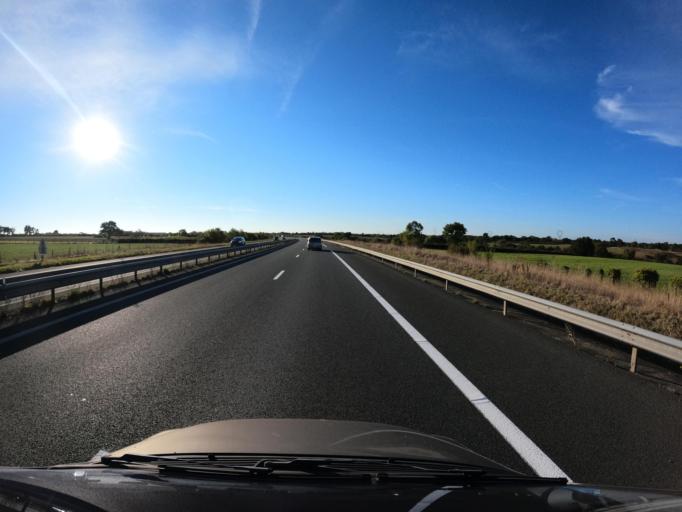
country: FR
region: Pays de la Loire
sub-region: Departement de Maine-et-Loire
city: Chemille-Melay
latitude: 47.2473
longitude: -0.6925
